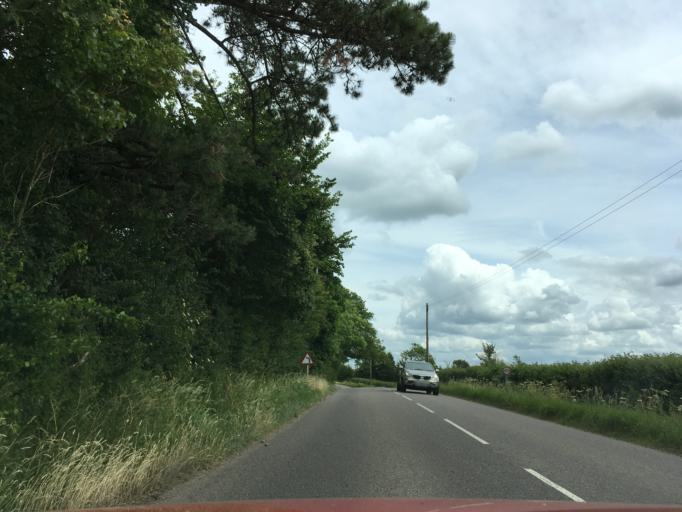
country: GB
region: England
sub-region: Wiltshire
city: Lyneham
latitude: 51.5626
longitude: -1.9692
